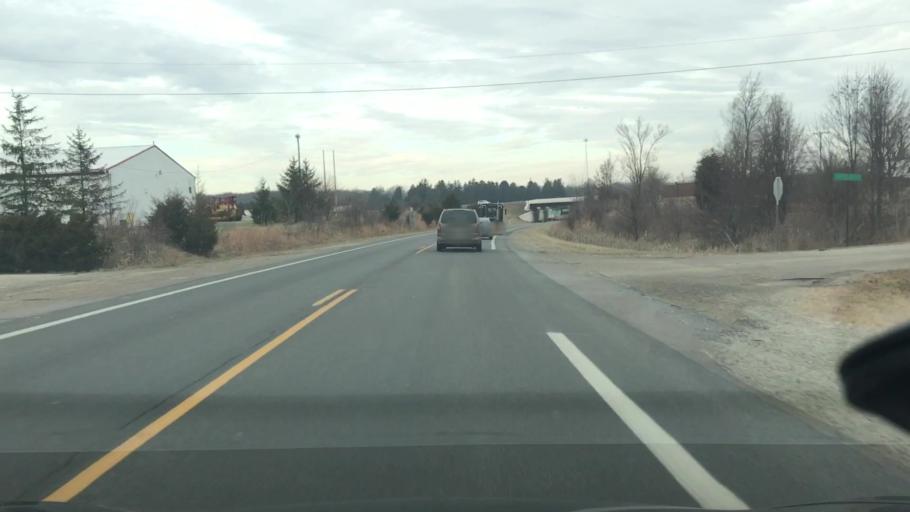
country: US
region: Ohio
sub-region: Madison County
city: Choctaw Lake
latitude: 39.9401
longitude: -83.4978
